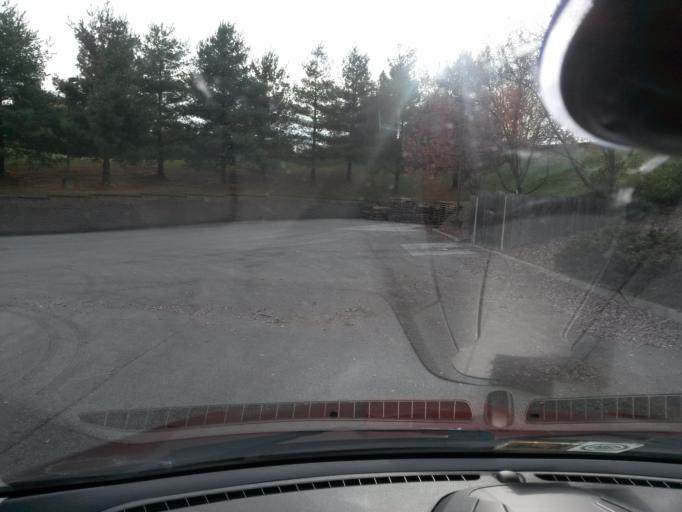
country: US
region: Virginia
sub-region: Roanoke County
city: Hollins
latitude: 37.3154
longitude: -79.9842
